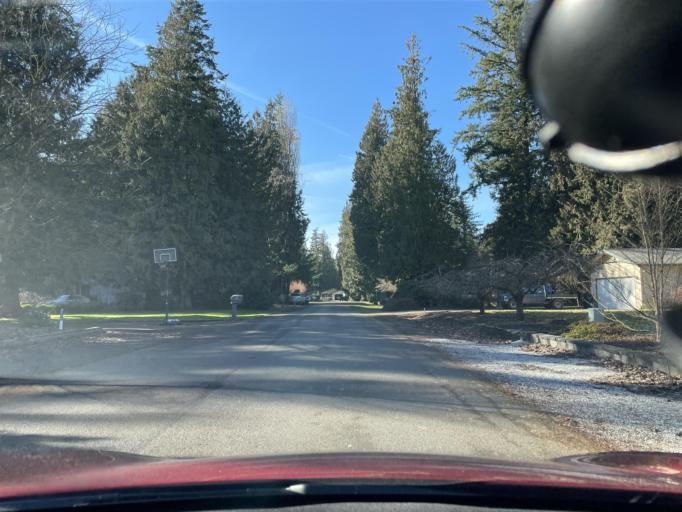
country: US
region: Washington
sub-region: Whatcom County
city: Lynden
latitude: 48.9523
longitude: -122.5104
